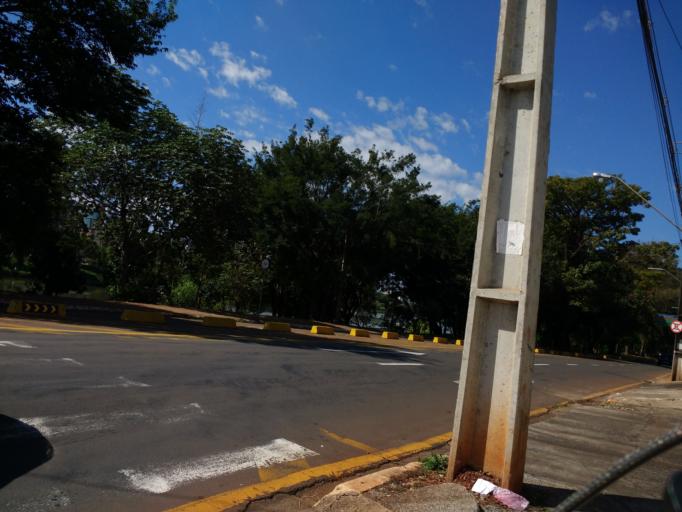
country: BR
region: Parana
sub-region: Londrina
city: Londrina
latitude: -23.3263
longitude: -51.1769
